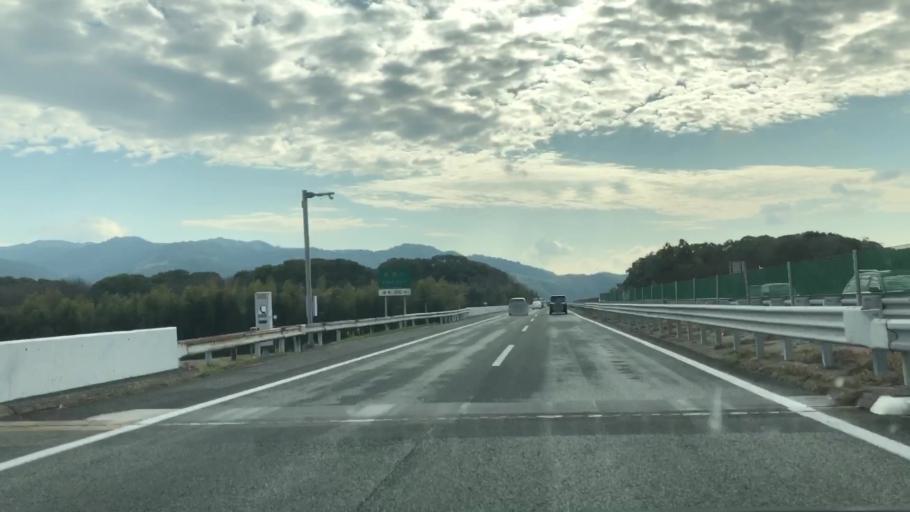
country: JP
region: Fukuoka
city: Setakamachi-takayanagi
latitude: 33.1840
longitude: 130.5186
